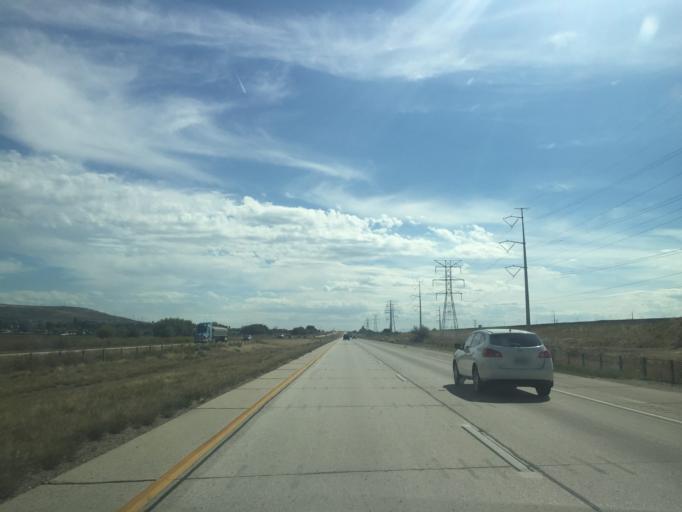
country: US
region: Utah
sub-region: Box Elder County
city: Willard
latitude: 41.3867
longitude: -112.0420
